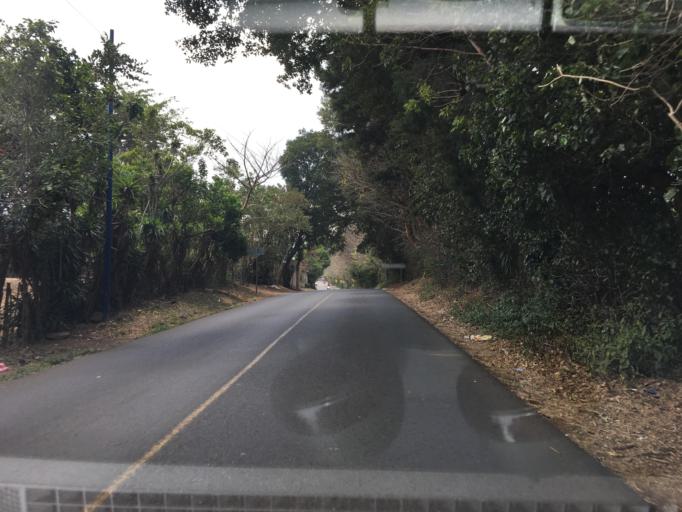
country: GT
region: Escuintla
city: San Vicente Pacaya
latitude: 14.3483
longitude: -90.5718
